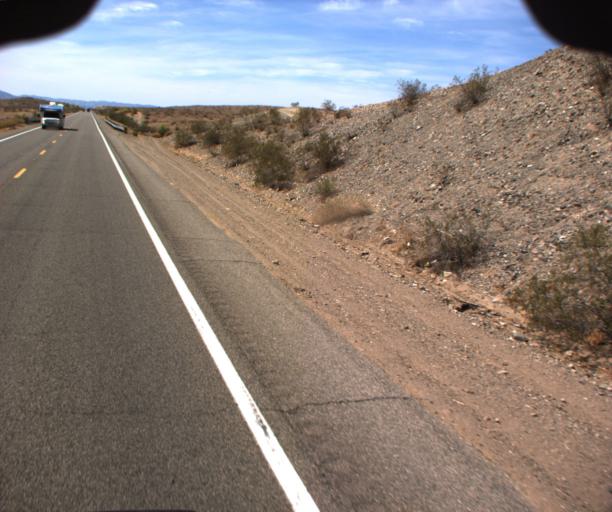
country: US
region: Arizona
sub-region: Mohave County
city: Lake Havasu City
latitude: 34.4352
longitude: -114.2211
